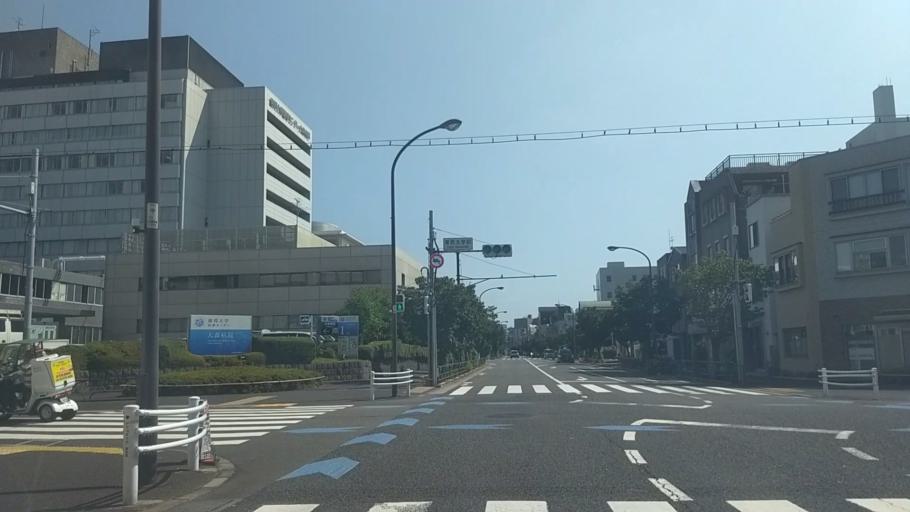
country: JP
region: Kanagawa
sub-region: Kawasaki-shi
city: Kawasaki
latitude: 35.5707
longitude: 139.7239
